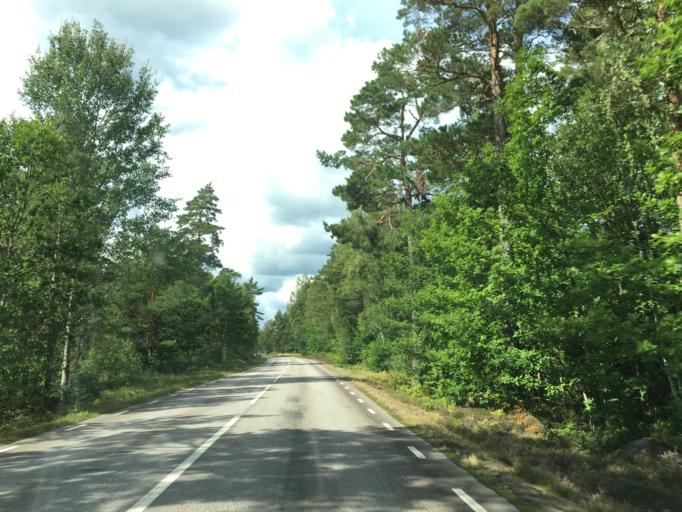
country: SE
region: Kalmar
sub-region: Nybro Kommun
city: Nybro
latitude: 56.9266
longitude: 15.9406
